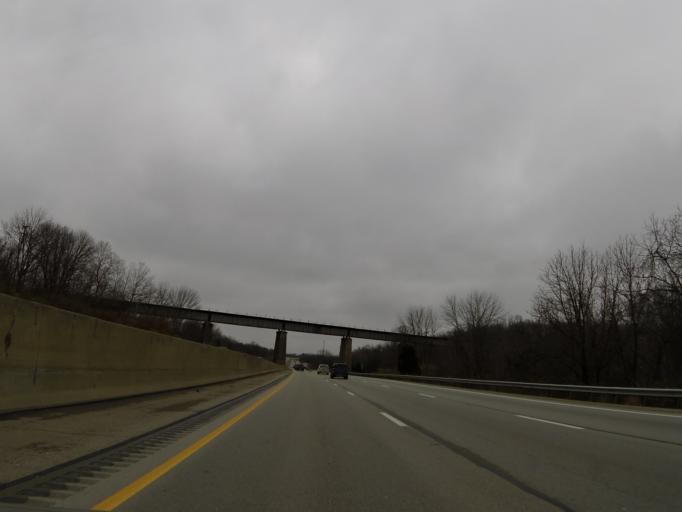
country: US
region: Kentucky
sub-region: Boone County
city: Walton
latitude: 38.8425
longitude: -84.6184
